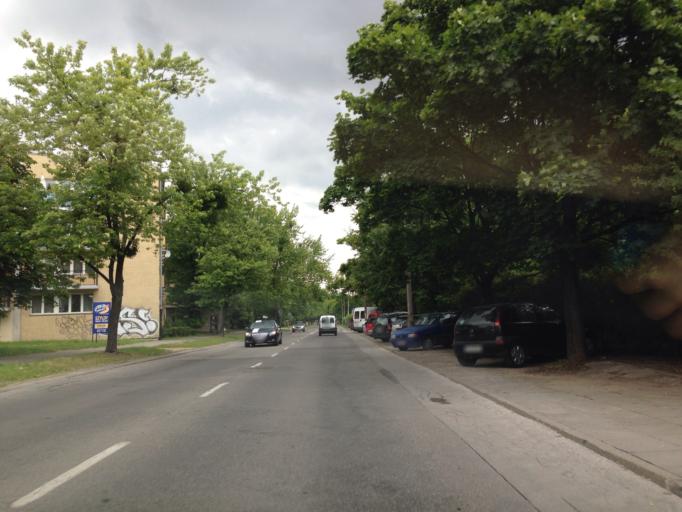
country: PL
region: Masovian Voivodeship
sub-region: Warszawa
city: Bielany
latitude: 52.2721
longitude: 20.9512
